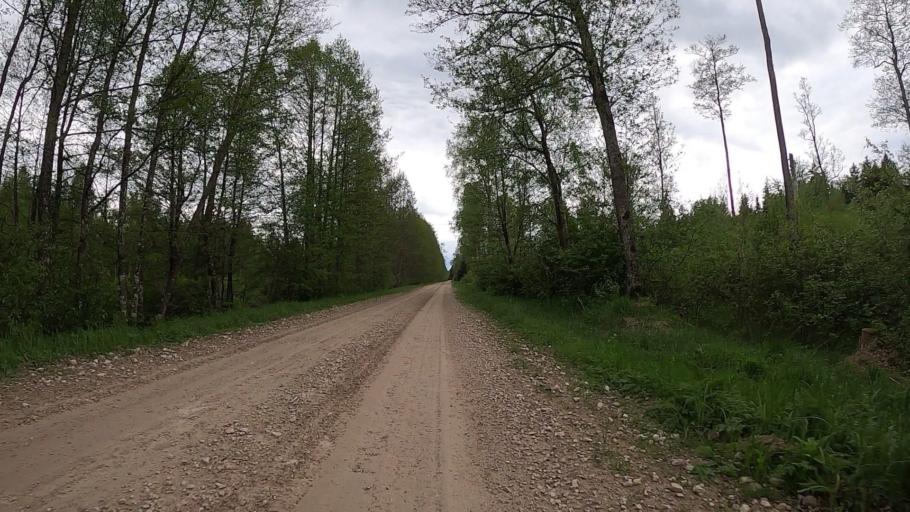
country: LV
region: Ozolnieku
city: Ozolnieki
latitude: 56.7844
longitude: 23.7697
